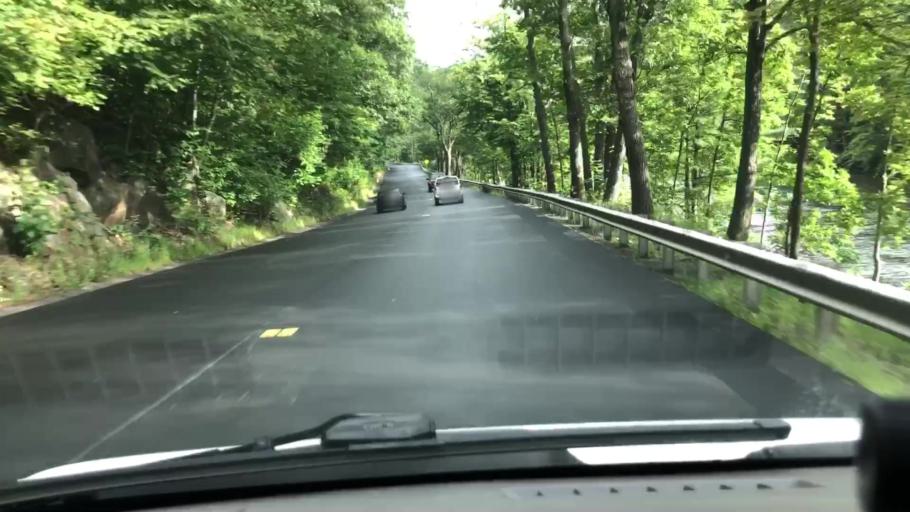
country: US
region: Massachusetts
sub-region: Franklin County
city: Charlemont
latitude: 42.6245
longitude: -72.8507
